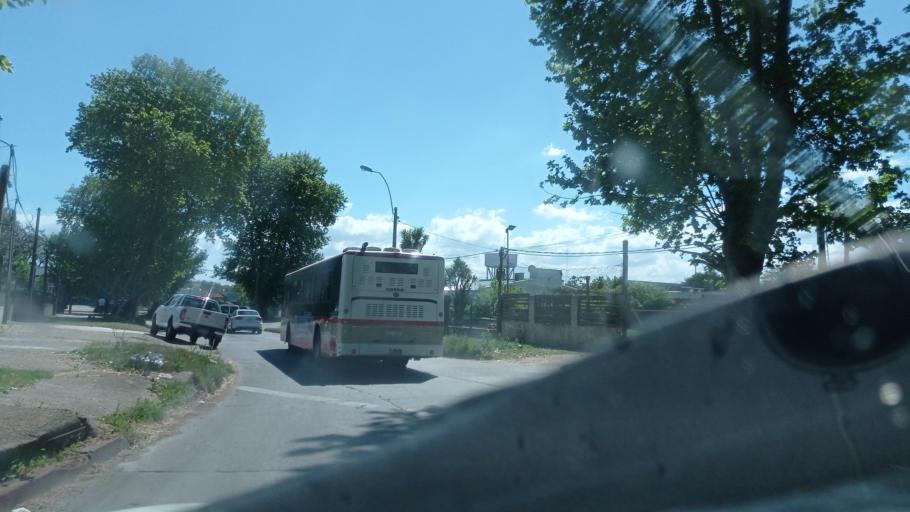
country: UY
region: Canelones
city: Paso de Carrasco
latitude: -34.8702
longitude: -56.1168
